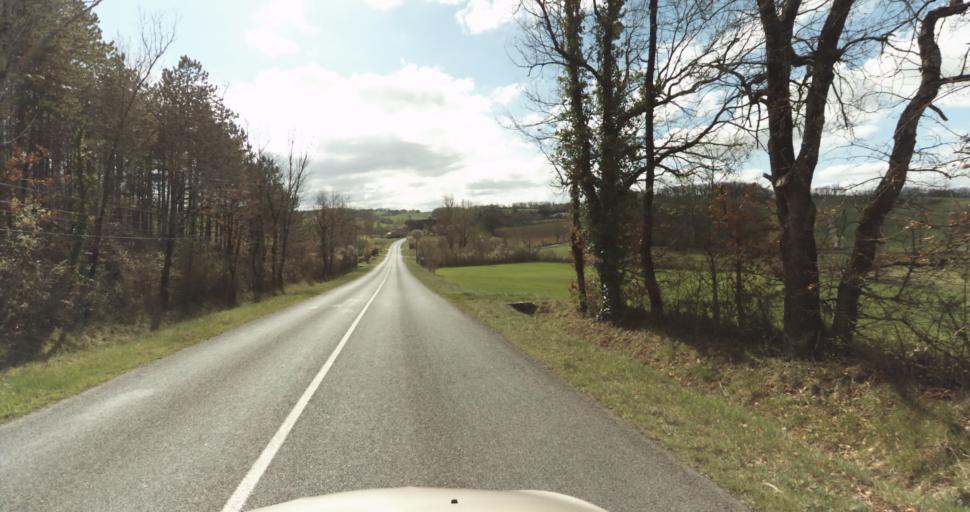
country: FR
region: Midi-Pyrenees
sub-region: Departement du Tarn
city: Puygouzon
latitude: 43.8794
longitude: 2.1549
